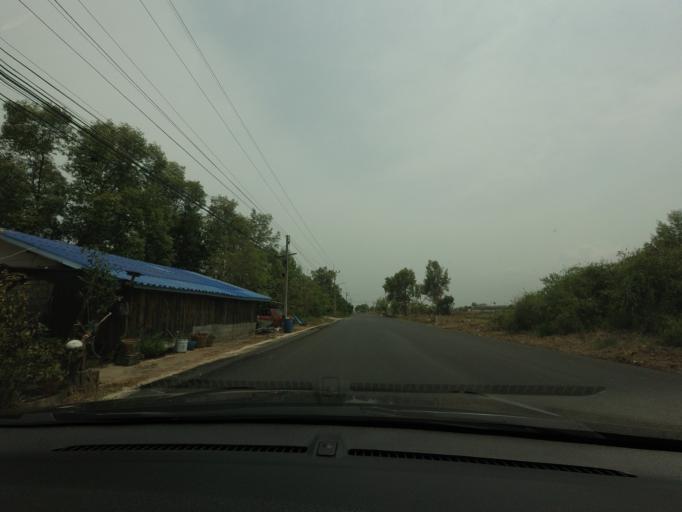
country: TH
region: Samut Songkhram
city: Amphawa
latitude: 13.3464
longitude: 99.9315
